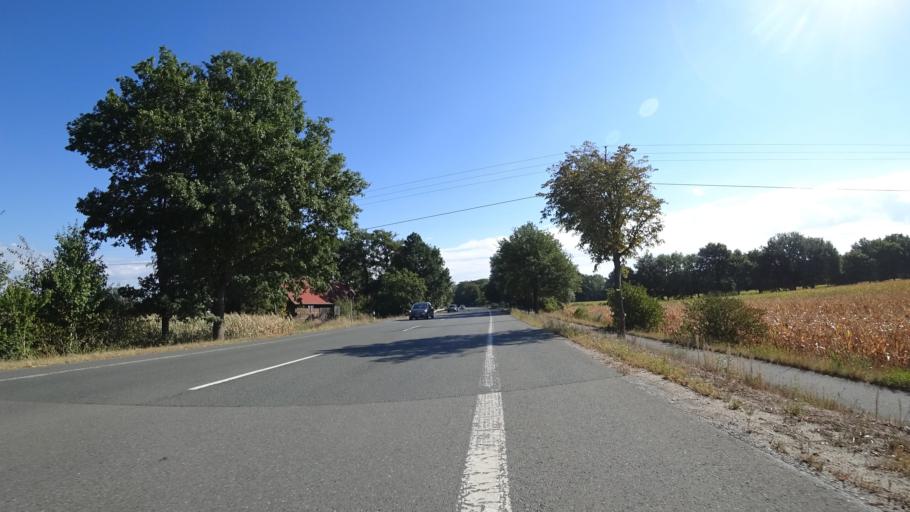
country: DE
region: North Rhine-Westphalia
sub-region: Regierungsbezirk Detmold
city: Rheda-Wiedenbruck
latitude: 51.8990
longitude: 8.3111
